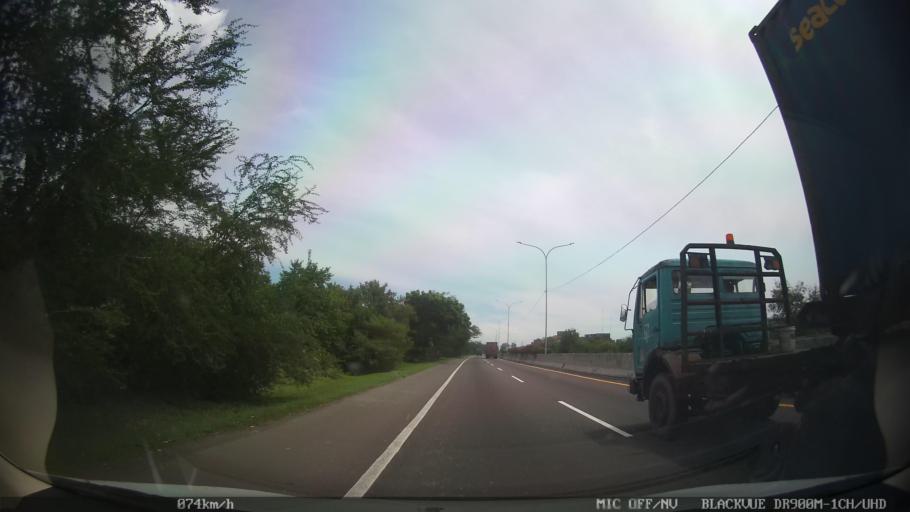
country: ID
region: North Sumatra
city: Belawan
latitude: 3.7645
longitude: 98.6834
